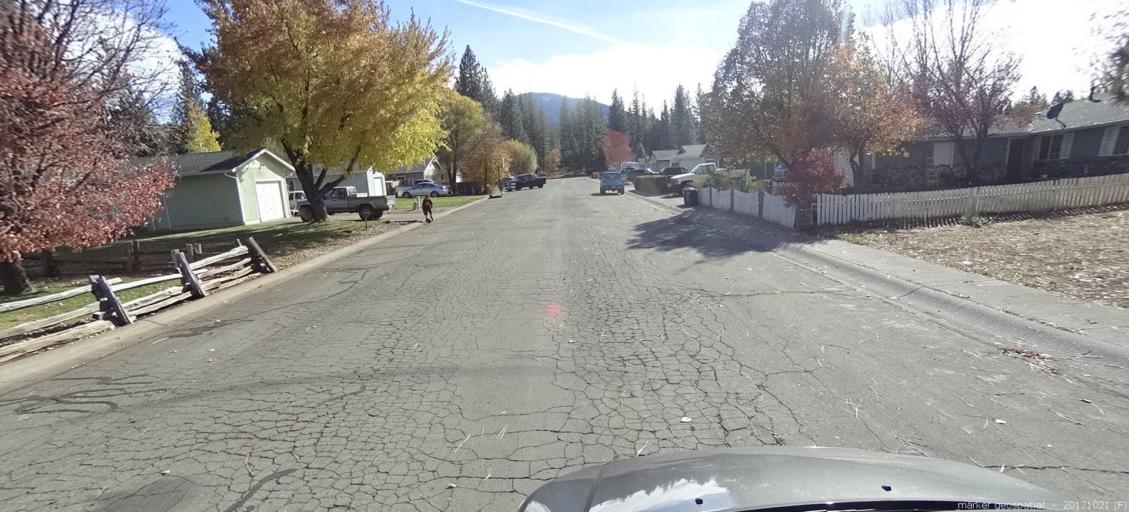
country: US
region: California
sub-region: Shasta County
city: Burney
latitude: 40.8827
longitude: -121.6477
